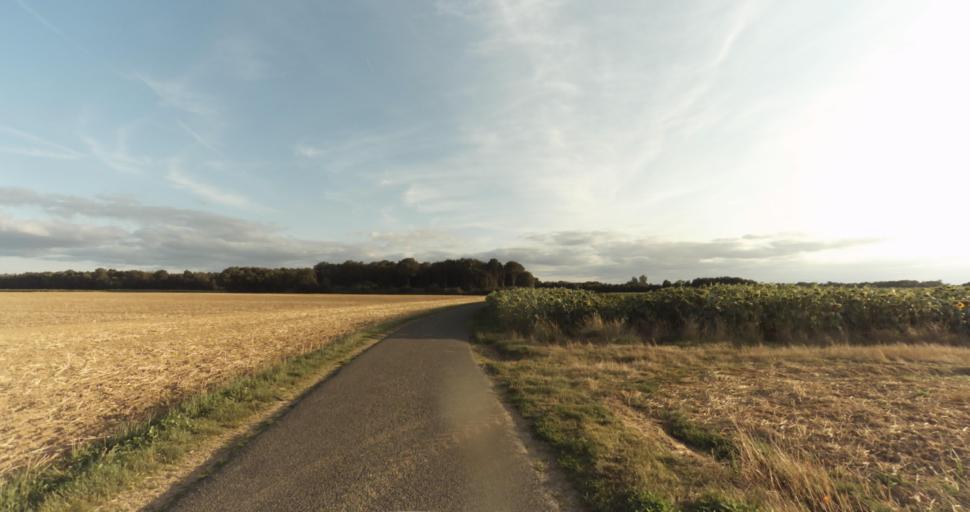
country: FR
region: Haute-Normandie
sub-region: Departement de l'Eure
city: Marcilly-sur-Eure
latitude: 48.8429
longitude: 1.2726
